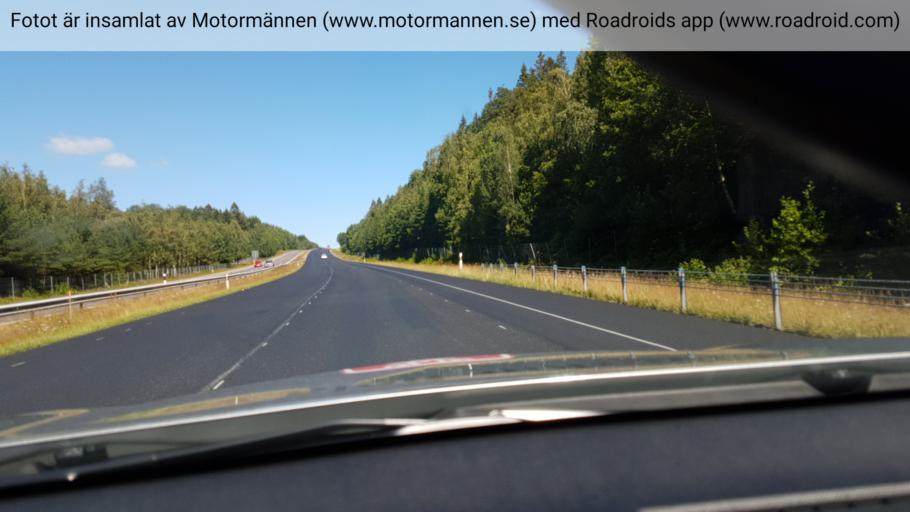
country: SE
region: Vaestra Goetaland
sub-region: Stenungsunds Kommun
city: Stenungsund
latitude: 58.0743
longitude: 11.8902
